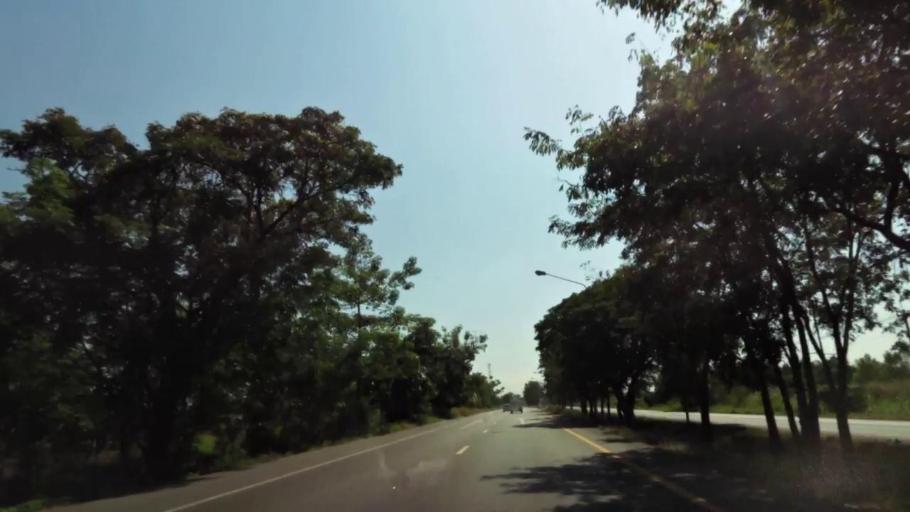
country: TH
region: Nakhon Sawan
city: Kao Liao
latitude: 15.8774
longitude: 100.1160
